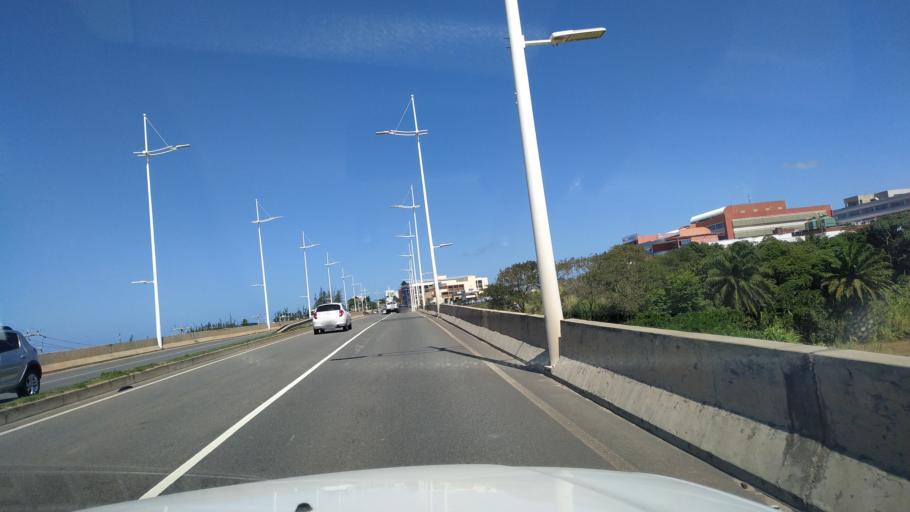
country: BR
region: Bahia
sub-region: Lauro De Freitas
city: Lauro de Freitas
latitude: -12.9365
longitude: -38.3854
